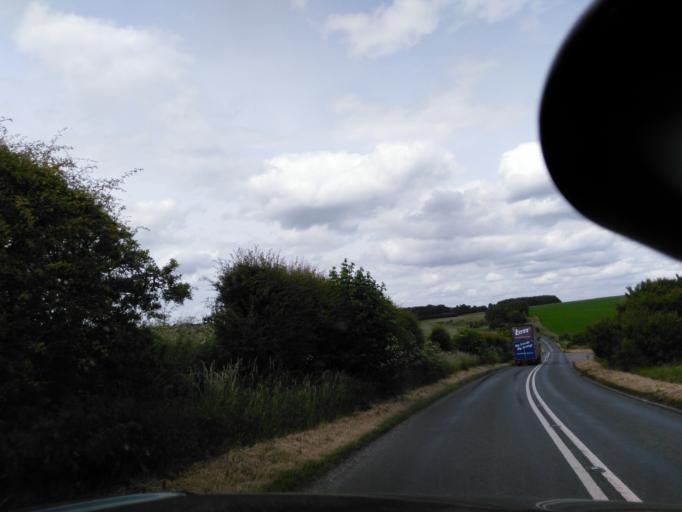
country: GB
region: England
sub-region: Wiltshire
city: Woodford
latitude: 51.1381
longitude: -1.8585
